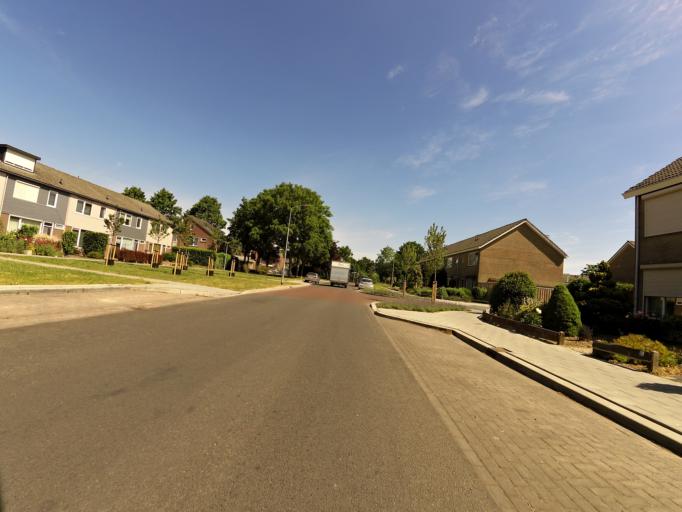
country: NL
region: Gelderland
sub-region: Gemeente Zevenaar
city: Zevenaar
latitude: 51.9330
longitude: 6.0647
